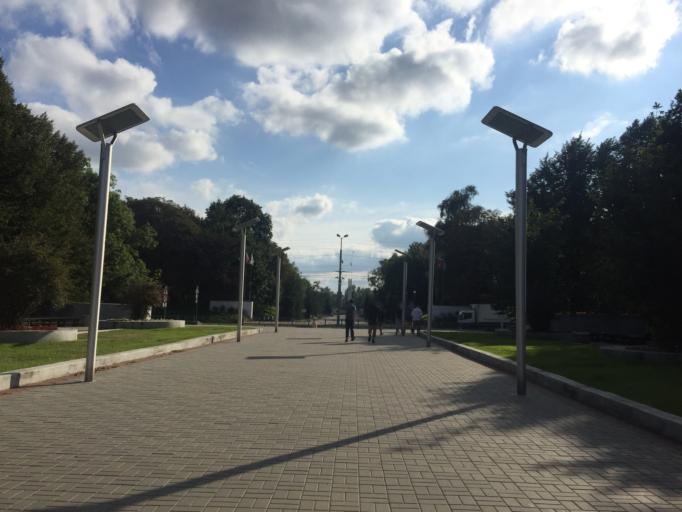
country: RU
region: Kaliningrad
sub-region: Gorod Kaliningrad
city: Kaliningrad
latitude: 54.6956
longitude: 20.5097
